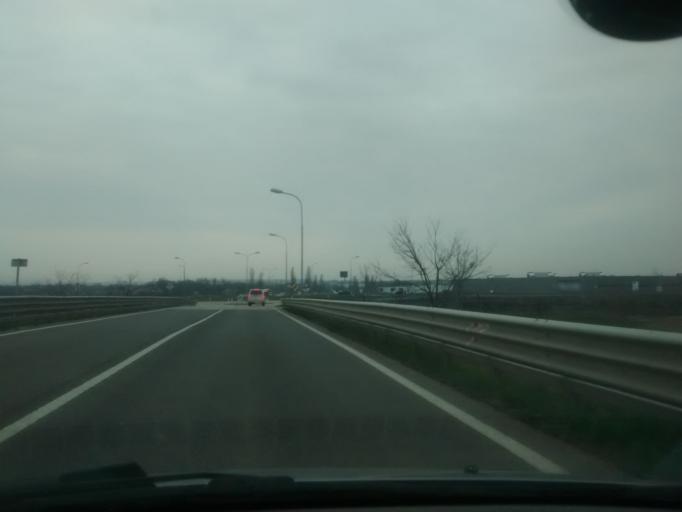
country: AT
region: Lower Austria
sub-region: Politischer Bezirk Modling
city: Achau
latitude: 48.0951
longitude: 16.3936
